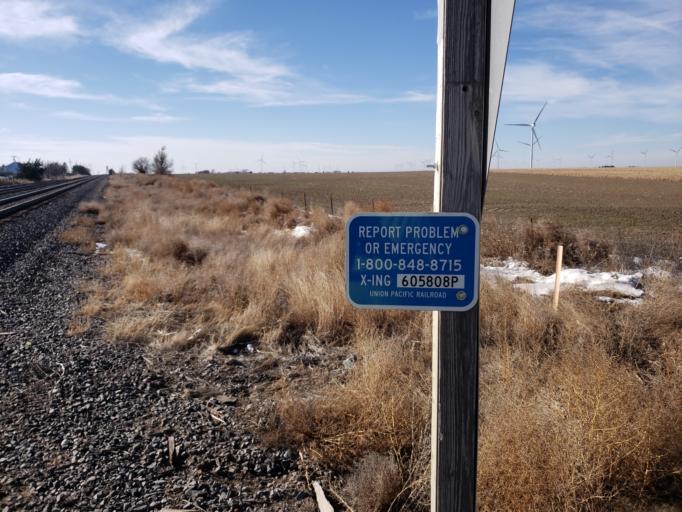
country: US
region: Kansas
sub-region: Ford County
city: Dodge City
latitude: 37.4881
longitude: -99.8975
